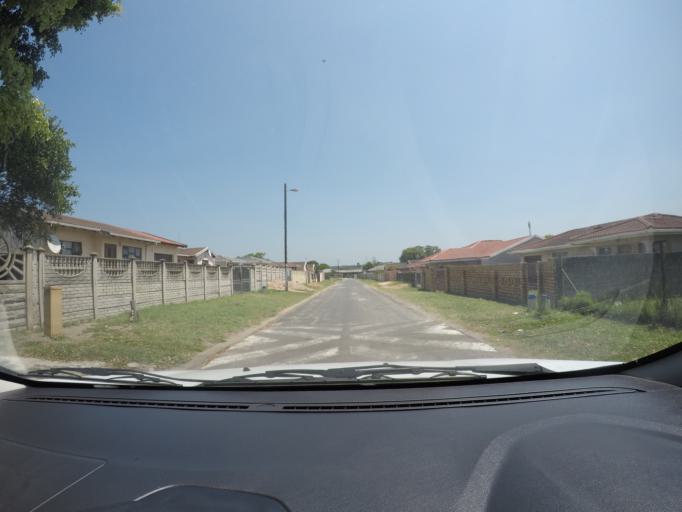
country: ZA
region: KwaZulu-Natal
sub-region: uThungulu District Municipality
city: eSikhawini
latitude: -28.8707
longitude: 31.9196
